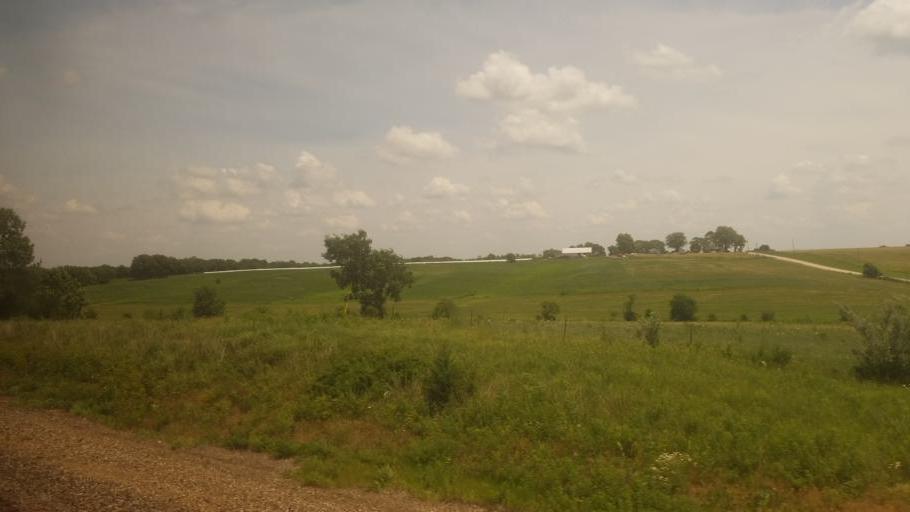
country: US
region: Missouri
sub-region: Macon County
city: La Plata
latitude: 40.0381
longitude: -92.4768
